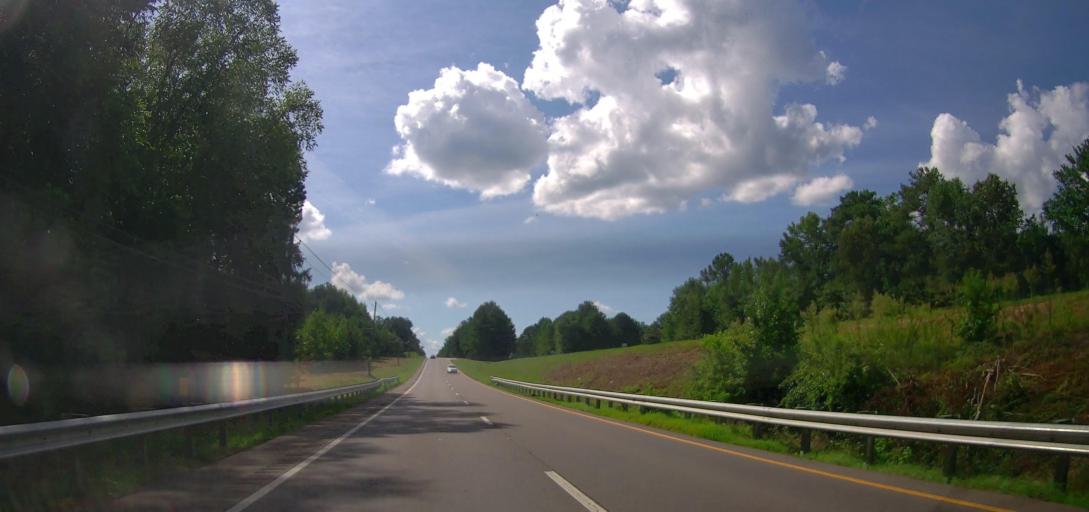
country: US
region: Alabama
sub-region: Tuscaloosa County
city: Northport
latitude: 33.2396
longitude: -87.6605
